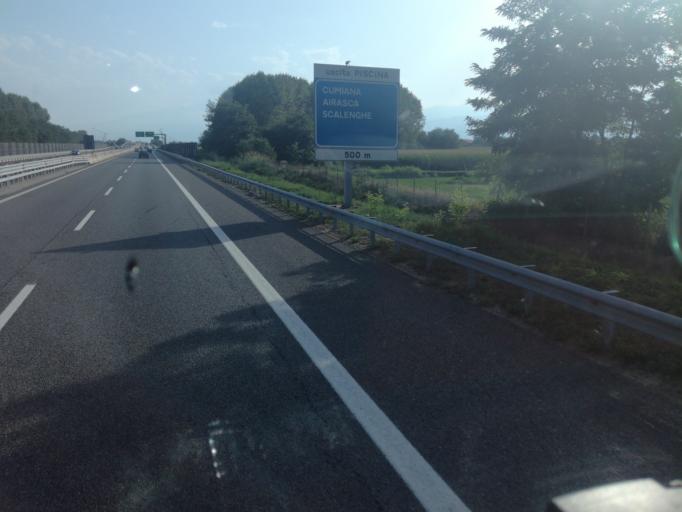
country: IT
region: Piedmont
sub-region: Provincia di Torino
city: Piscina
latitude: 44.9210
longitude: 7.4537
